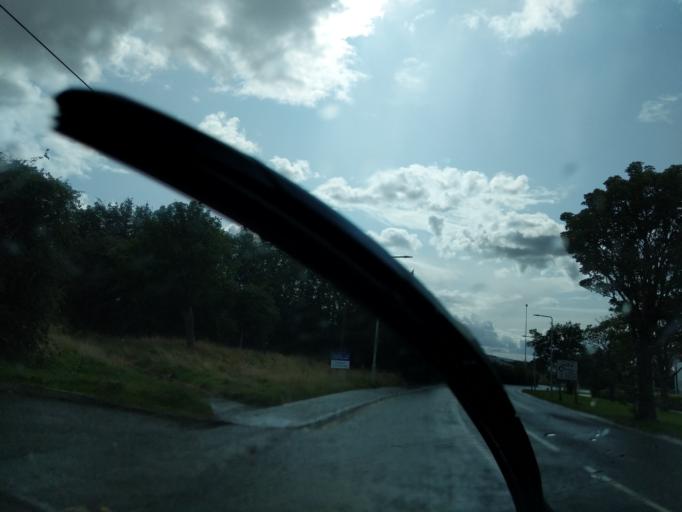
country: GB
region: Scotland
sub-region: Fife
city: Rosyth
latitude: 56.0290
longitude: -3.4291
